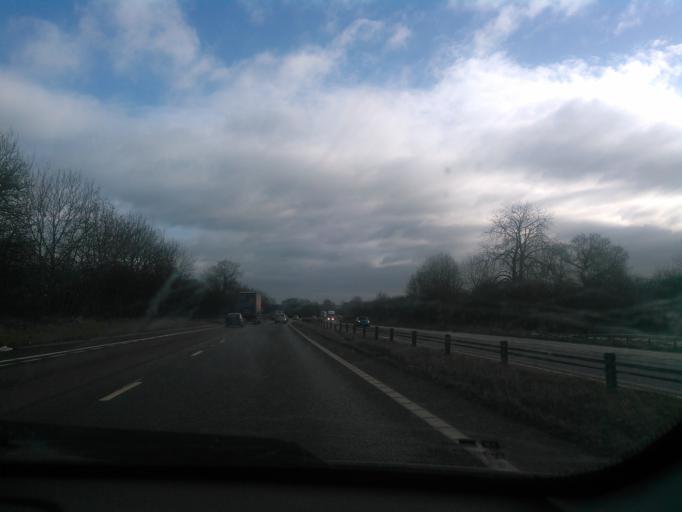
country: GB
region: England
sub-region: Staffordshire
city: Uttoxeter
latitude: 52.8916
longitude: -1.7685
